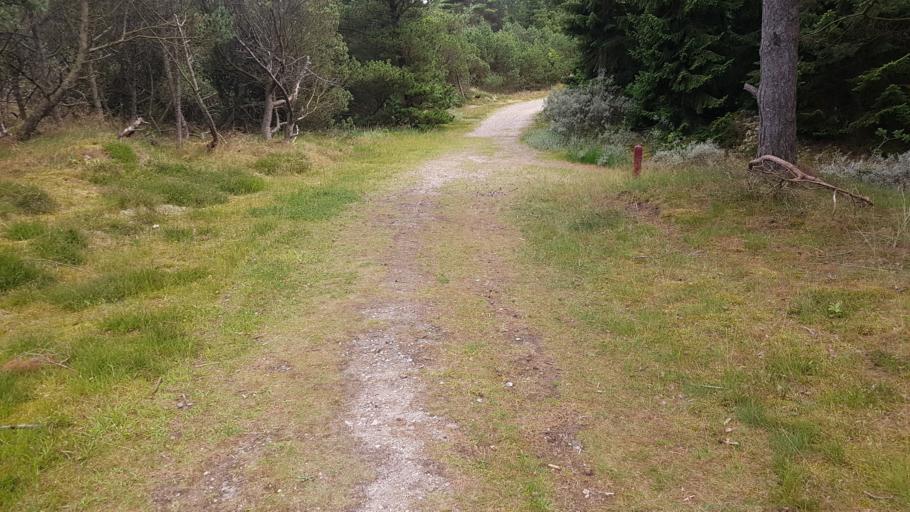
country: DE
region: Schleswig-Holstein
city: List
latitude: 55.1039
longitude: 8.5289
